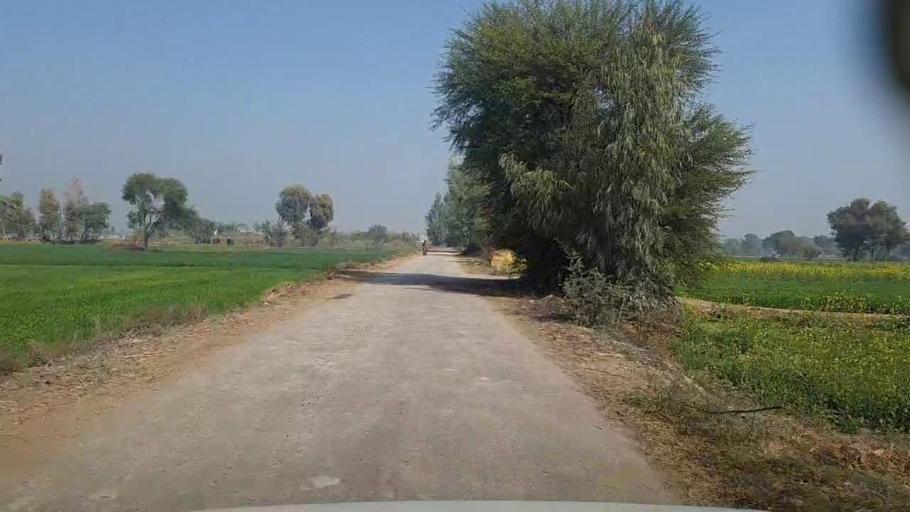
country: PK
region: Sindh
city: Khairpur
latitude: 27.9392
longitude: 69.6636
